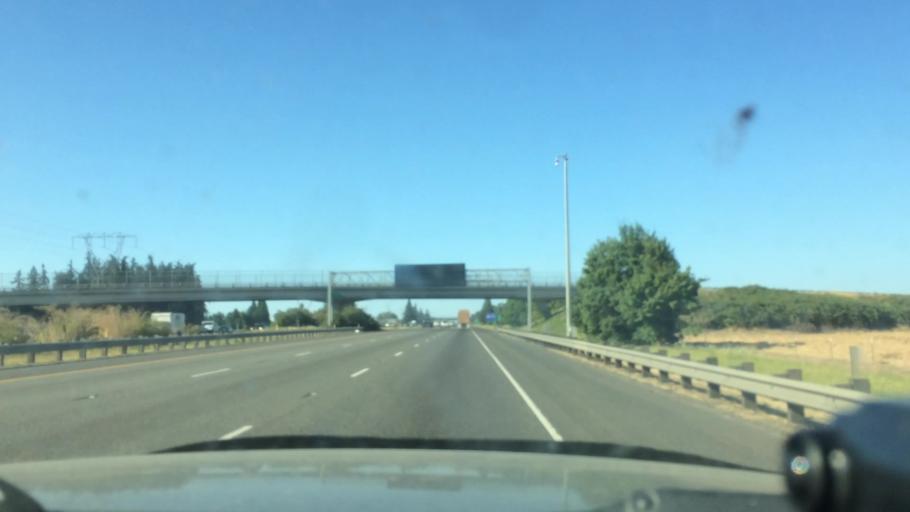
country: US
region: Oregon
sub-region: Marion County
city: Hayesville
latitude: 45.0269
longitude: -122.9847
